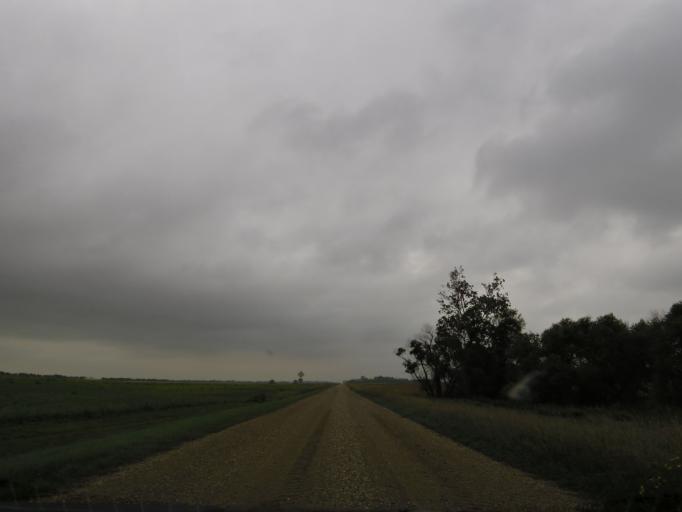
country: US
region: North Dakota
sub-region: Walsh County
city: Grafton
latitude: 48.4711
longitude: -97.1687
